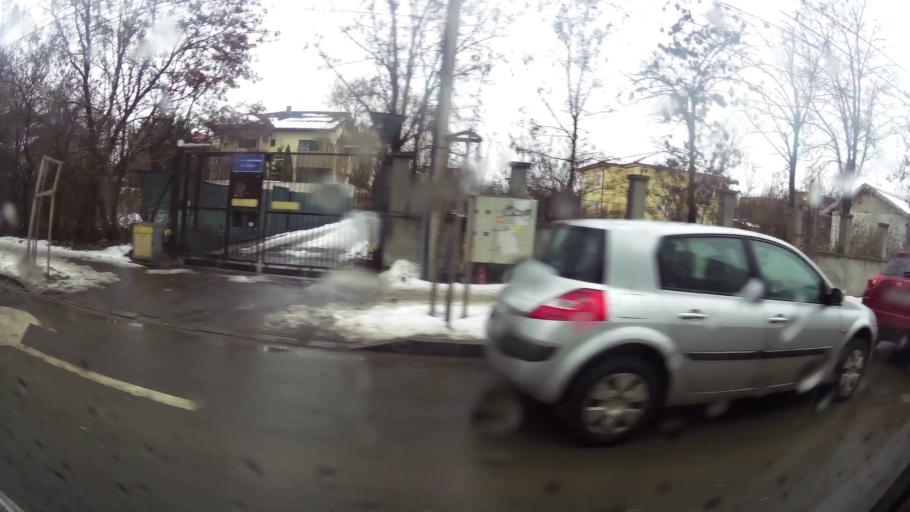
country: RO
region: Ilfov
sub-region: Comuna Chiajna
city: Rosu
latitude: 44.4186
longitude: 26.0096
